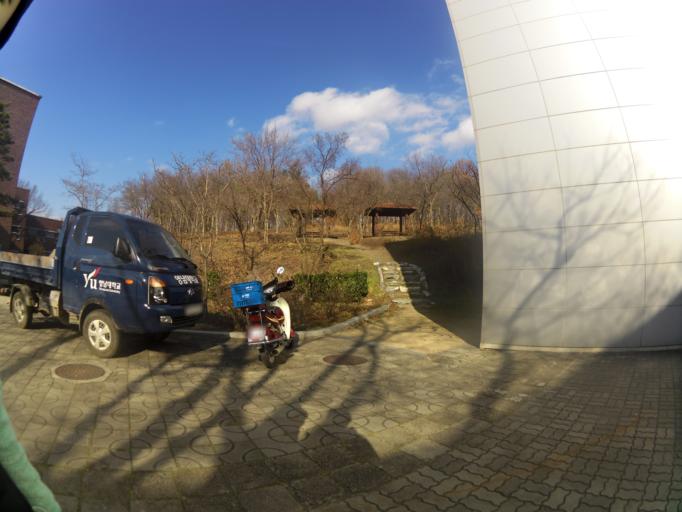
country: KR
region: Gyeongsangbuk-do
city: Gyeongsan-si
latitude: 35.8348
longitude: 128.7580
